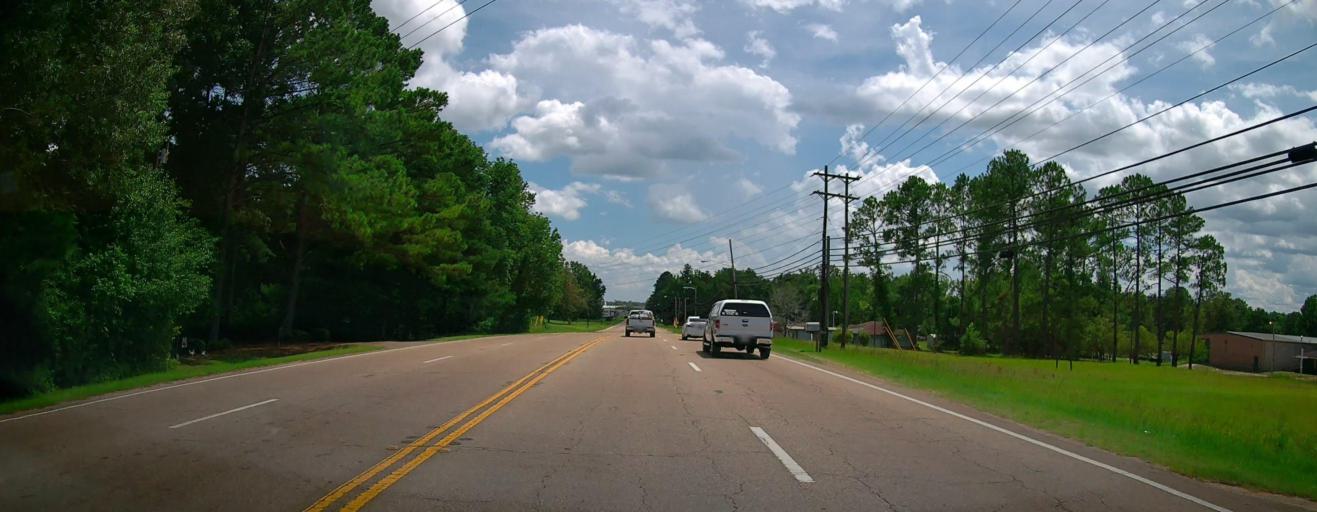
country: US
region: Mississippi
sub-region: Lee County
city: Verona
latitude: 34.1748
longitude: -88.7197
